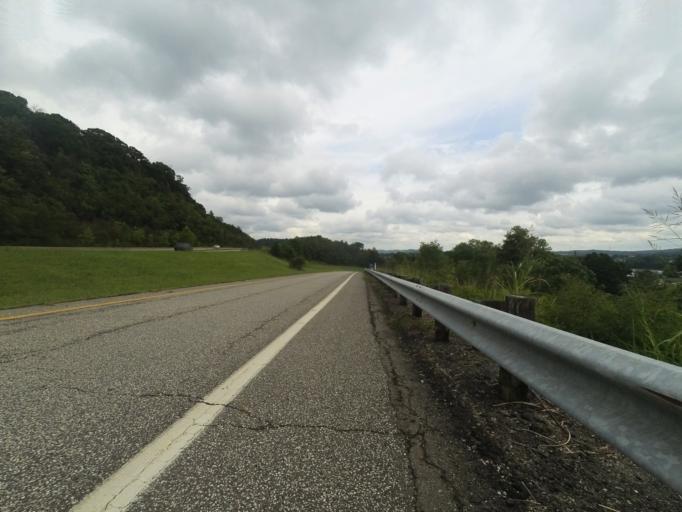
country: US
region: West Virginia
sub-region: Cabell County
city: Huntington
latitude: 38.4278
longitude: -82.4671
